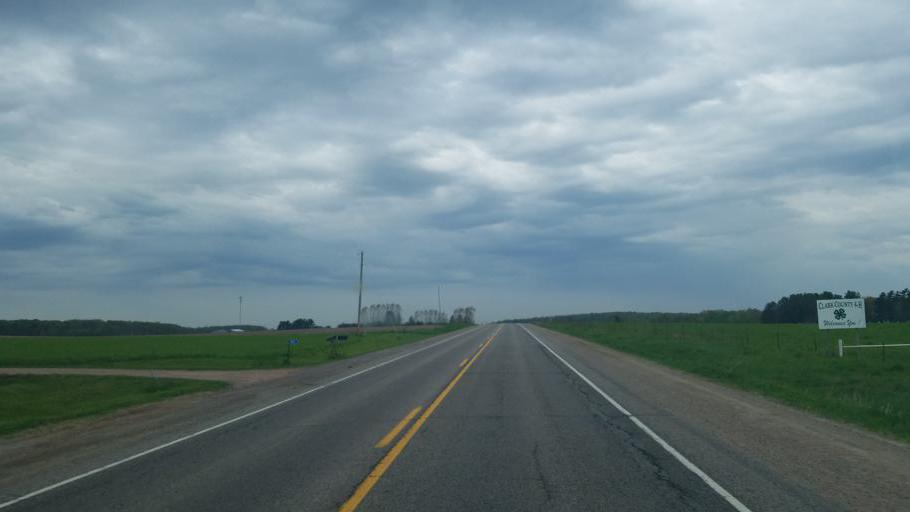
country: US
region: Wisconsin
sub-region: Marathon County
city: Spencer
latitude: 44.5991
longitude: -90.3181
